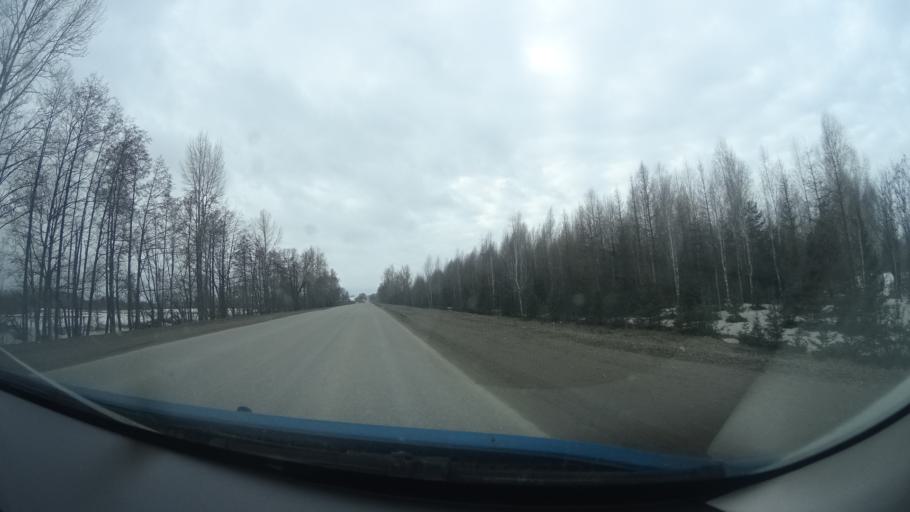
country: RU
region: Bashkortostan
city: Birsk
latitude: 55.4690
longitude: 55.5950
